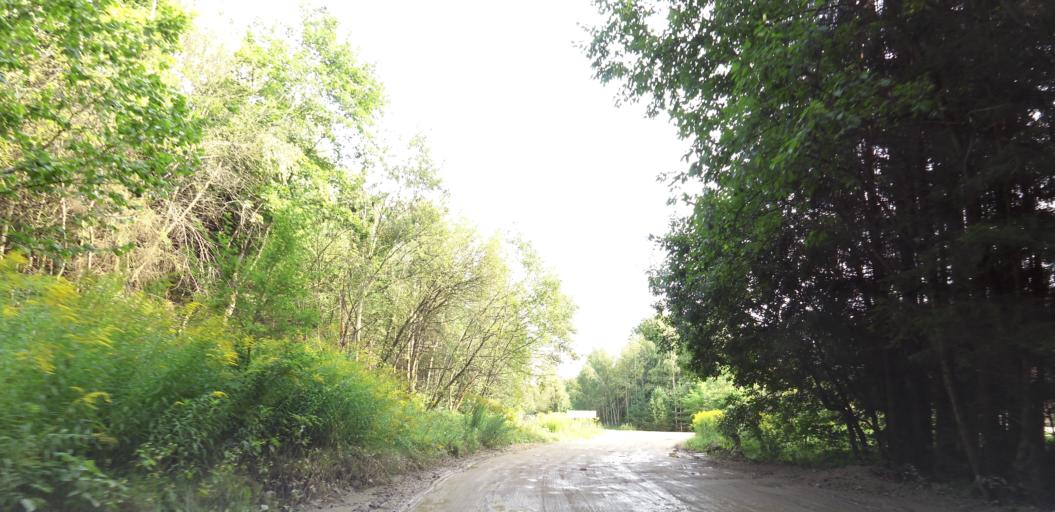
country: LT
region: Vilnius County
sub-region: Vilnius
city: Fabijoniskes
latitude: 54.7504
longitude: 25.2444
